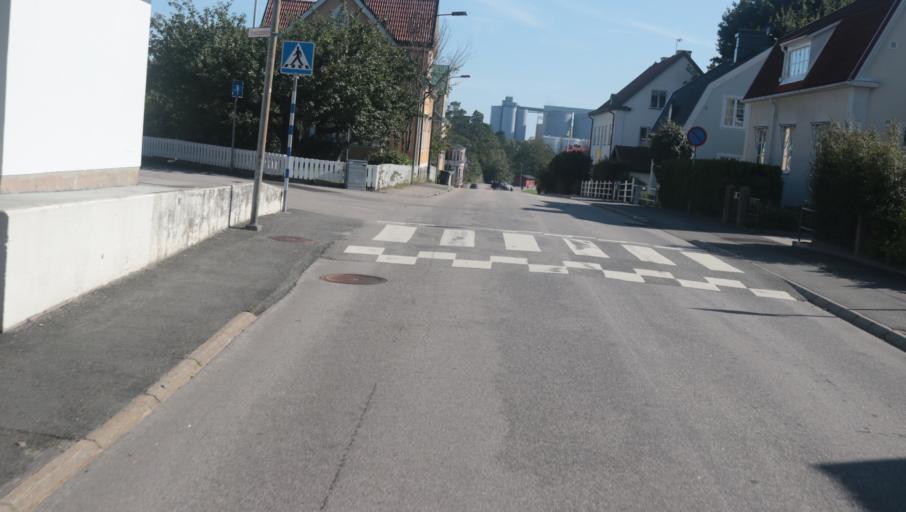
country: SE
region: Blekinge
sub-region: Karlshamns Kommun
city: Karlshamn
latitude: 56.1723
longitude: 14.8528
